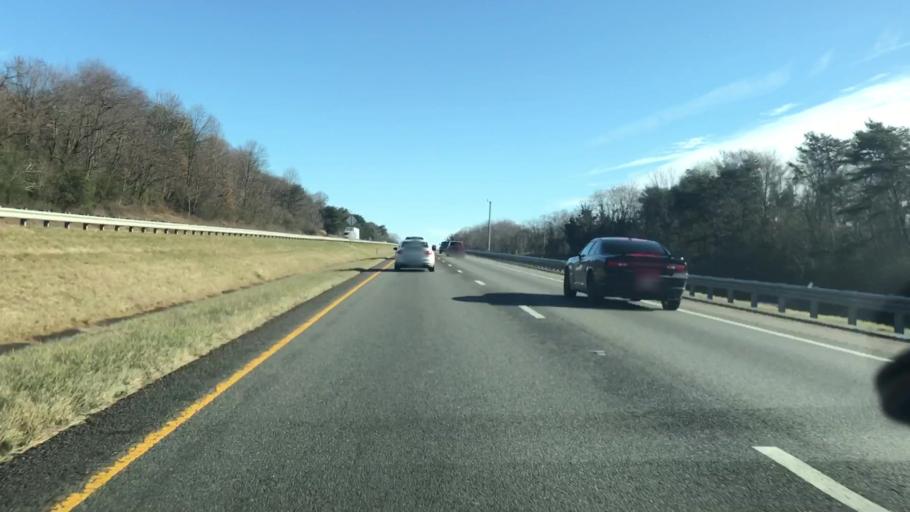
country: US
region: Virginia
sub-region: City of Salem
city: Salem
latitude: 37.2937
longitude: -80.0962
